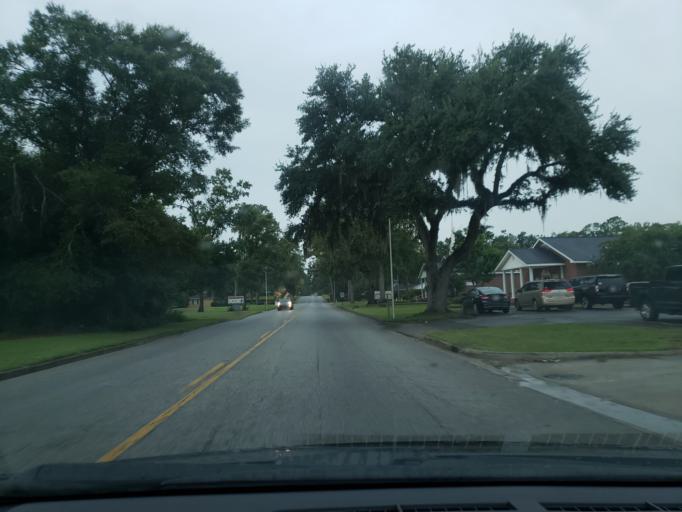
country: US
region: Georgia
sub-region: Dougherty County
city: Albany
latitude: 31.6050
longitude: -84.1837
